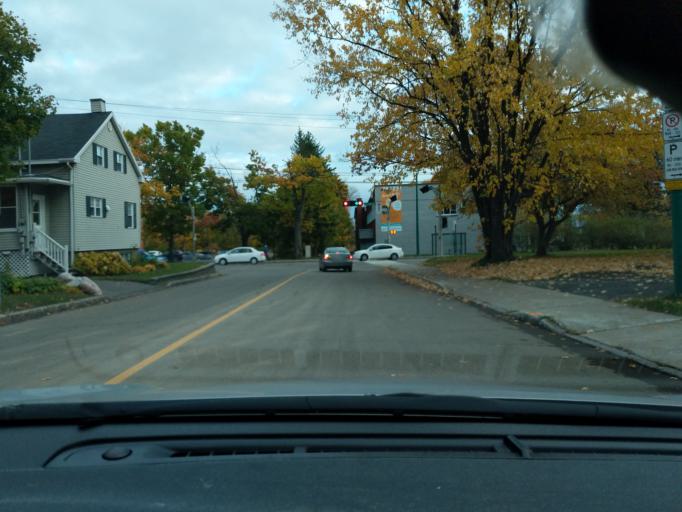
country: CA
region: Quebec
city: L'Ancienne-Lorette
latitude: 46.7595
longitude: -71.2876
